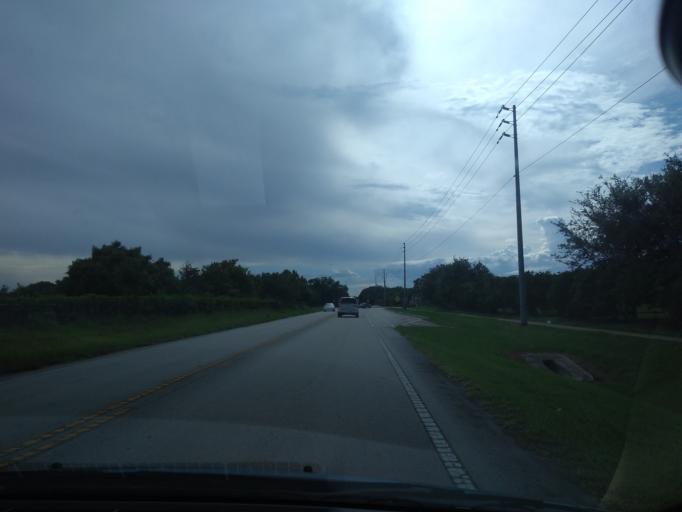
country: US
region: Florida
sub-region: Indian River County
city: West Vero Corridor
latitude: 27.6351
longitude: -80.4491
